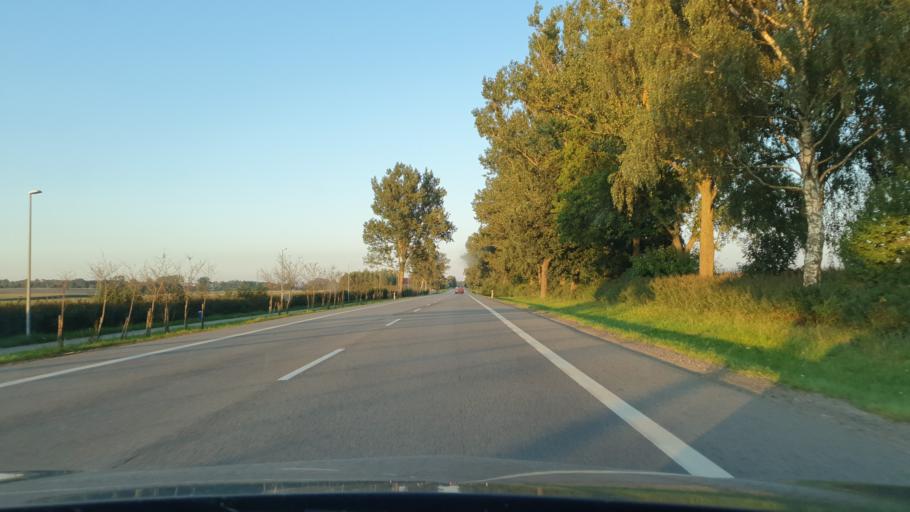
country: PL
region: Pomeranian Voivodeship
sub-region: Powiat slupski
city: Potegowo
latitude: 54.4694
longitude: 17.4738
